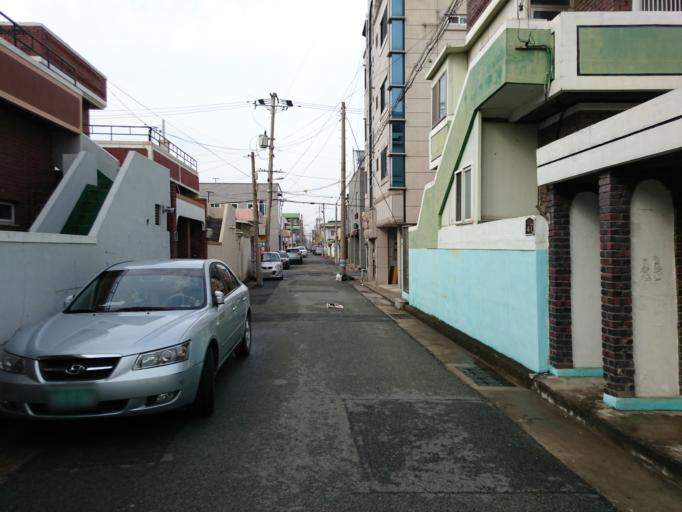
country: KR
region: Gyeongsangbuk-do
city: Pohang
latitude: 36.0245
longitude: 129.3736
